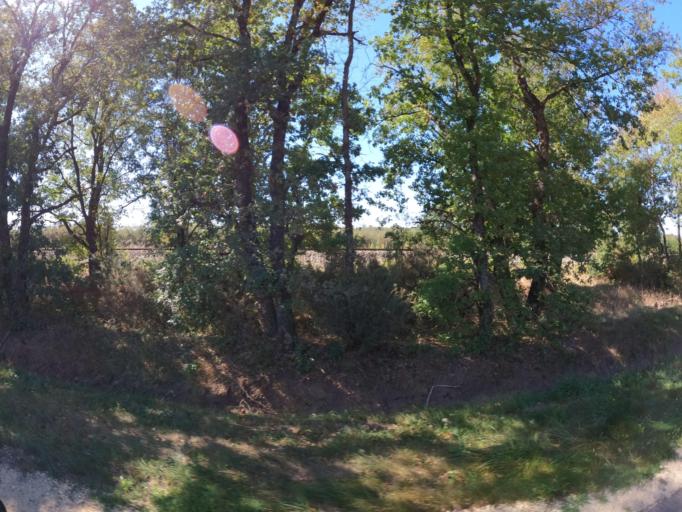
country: FR
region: Poitou-Charentes
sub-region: Departement de la Vienne
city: Saulge
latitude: 46.3859
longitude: 0.9140
